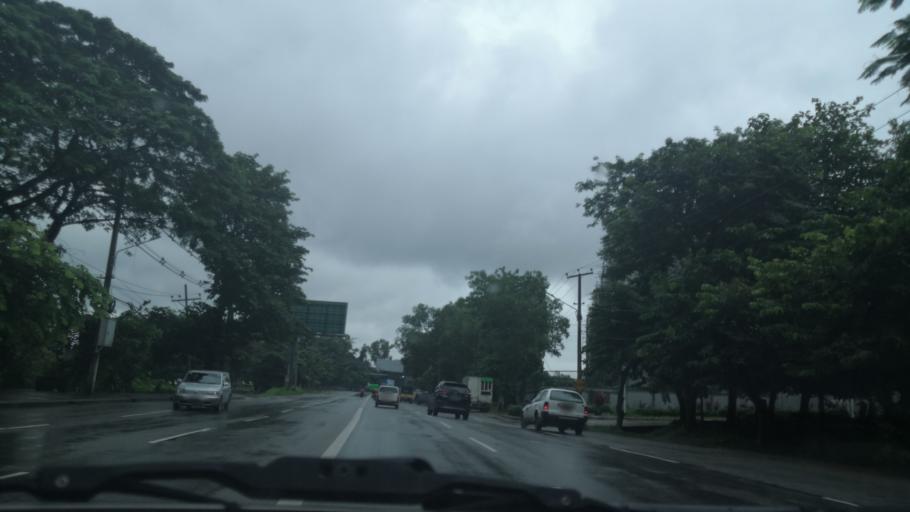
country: MM
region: Yangon
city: Yangon
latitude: 16.8983
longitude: 96.1235
